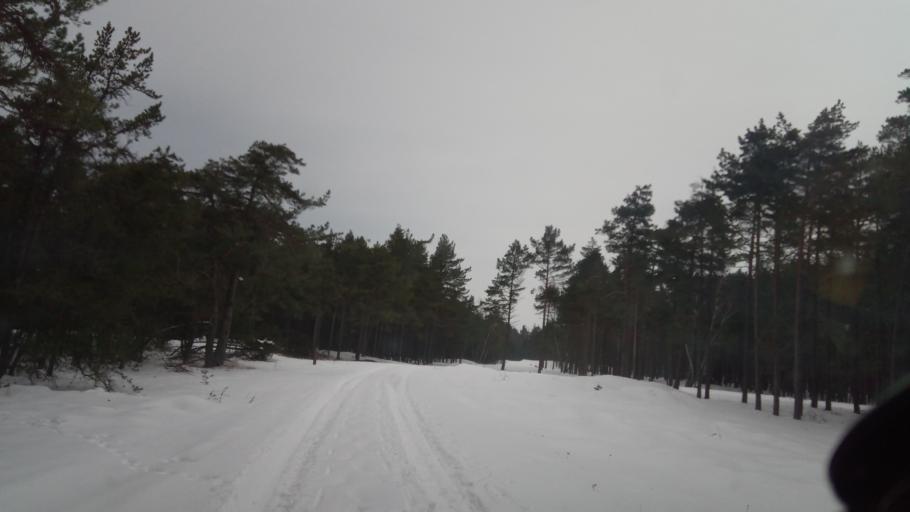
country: LT
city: Neringa
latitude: 55.4237
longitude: 21.0942
